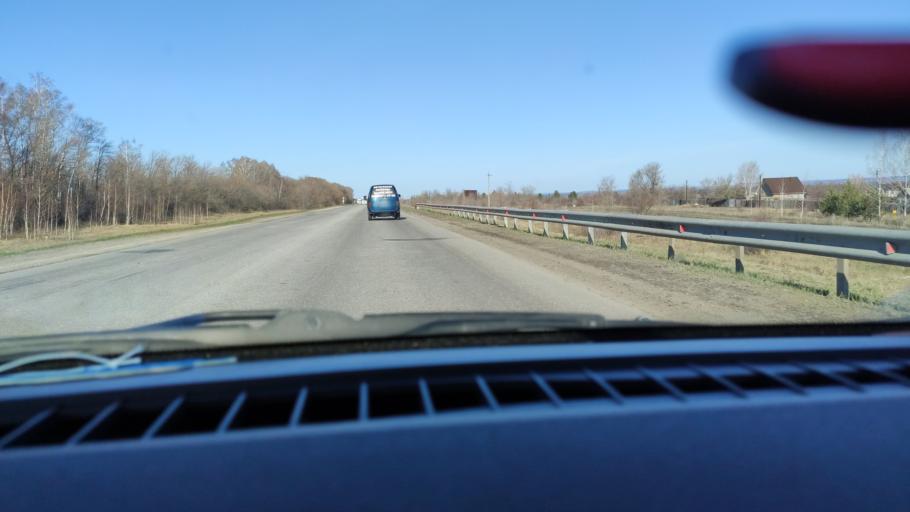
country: RU
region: Samara
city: Varlamovo
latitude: 53.1220
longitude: 48.3150
